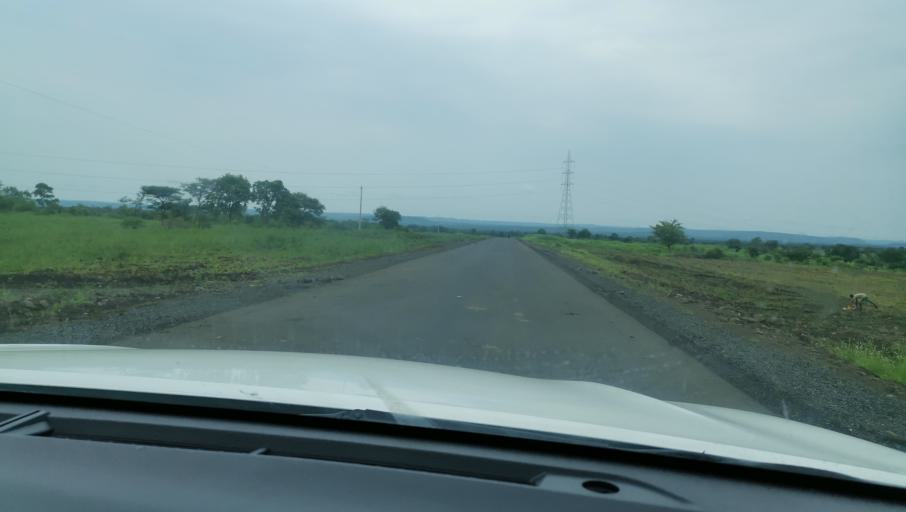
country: SD
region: Al Qadarif
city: Doka
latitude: 12.9014
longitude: 36.2228
